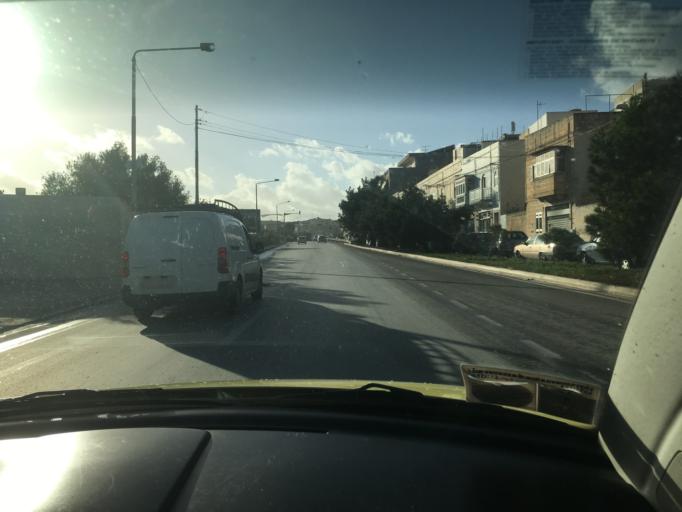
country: MT
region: Qormi
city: Qormi
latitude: 35.8752
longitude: 14.4729
